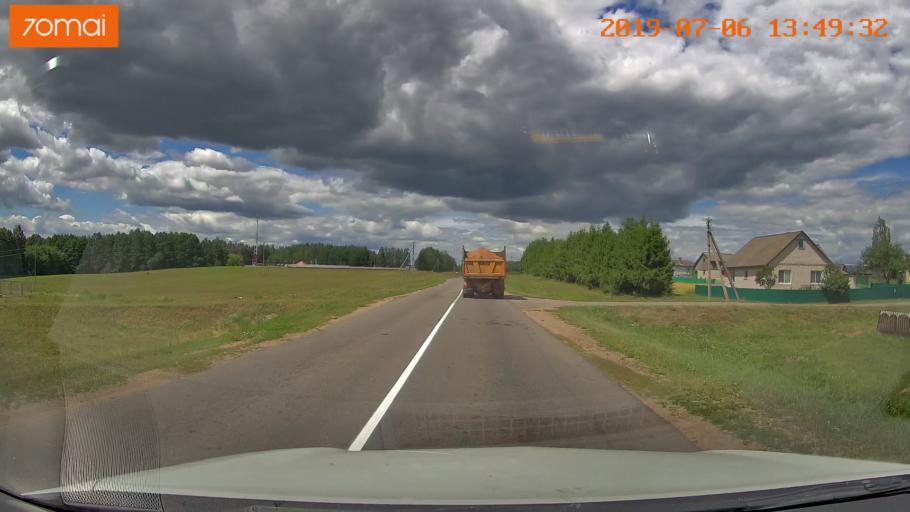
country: BY
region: Minsk
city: Ivyanyets
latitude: 53.6944
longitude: 26.8511
